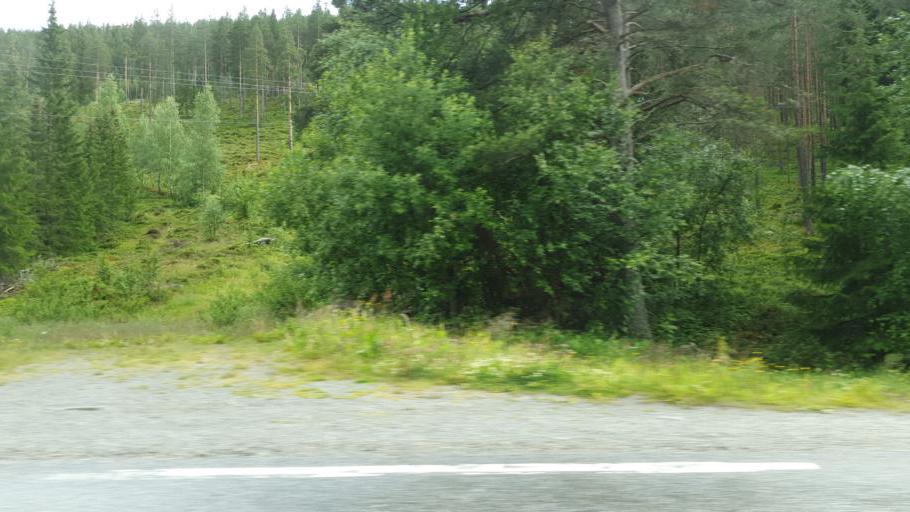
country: NO
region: Oppland
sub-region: Dovre
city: Dovre
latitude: 61.8565
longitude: 9.2545
